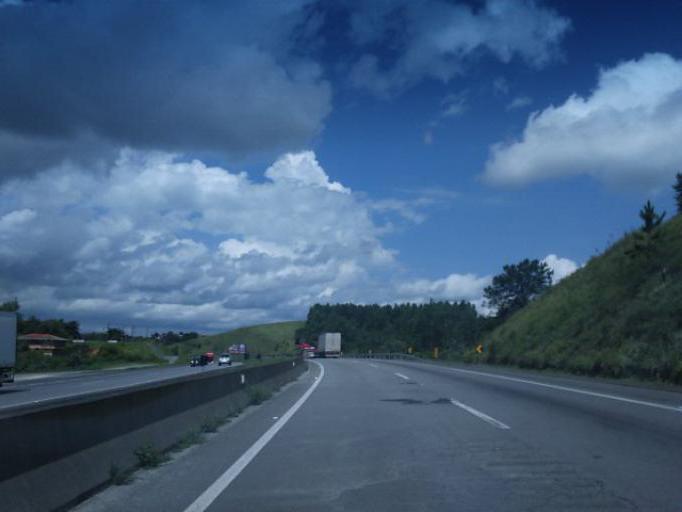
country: BR
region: Sao Paulo
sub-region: Cajati
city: Cajati
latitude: -24.7432
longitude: -48.1335
